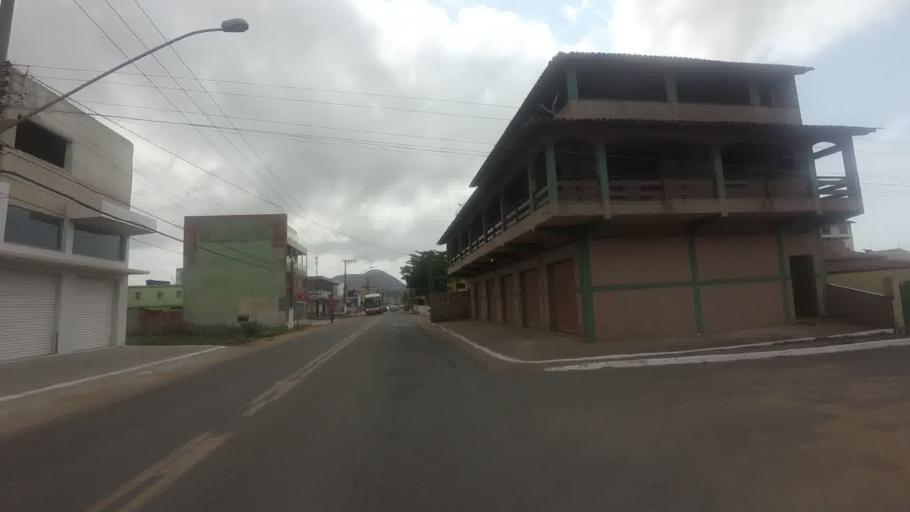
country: BR
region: Espirito Santo
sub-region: Piuma
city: Piuma
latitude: -20.9003
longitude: -40.7781
